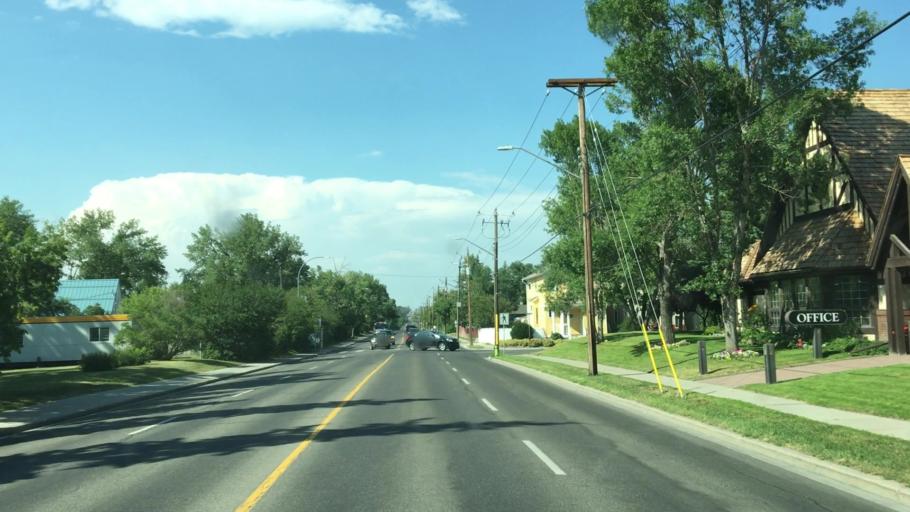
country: CA
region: Alberta
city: Calgary
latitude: 51.0809
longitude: -114.0715
